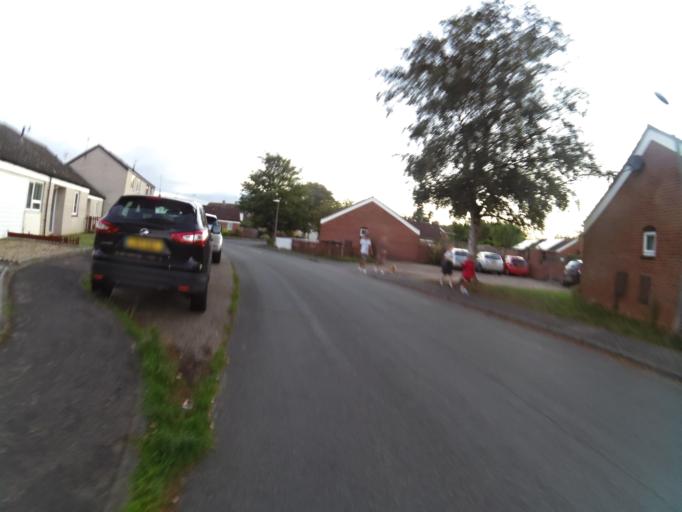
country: GB
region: England
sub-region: Suffolk
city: Bramford
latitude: 52.0806
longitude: 1.0980
